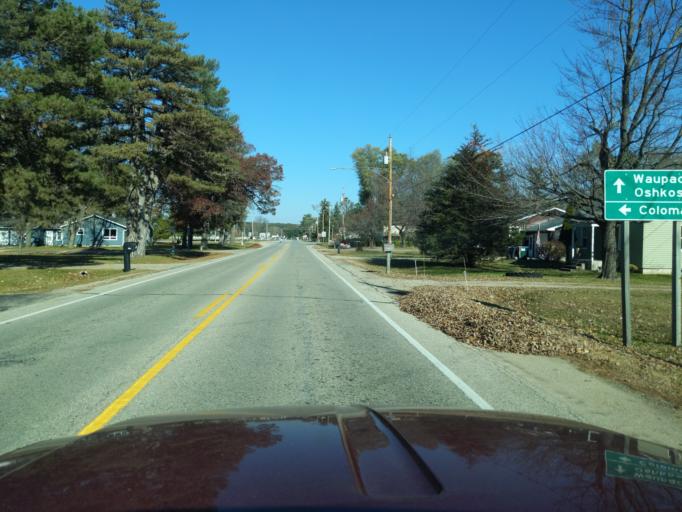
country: US
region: Wisconsin
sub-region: Waushara County
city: Wautoma
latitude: 44.0669
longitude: -89.2975
